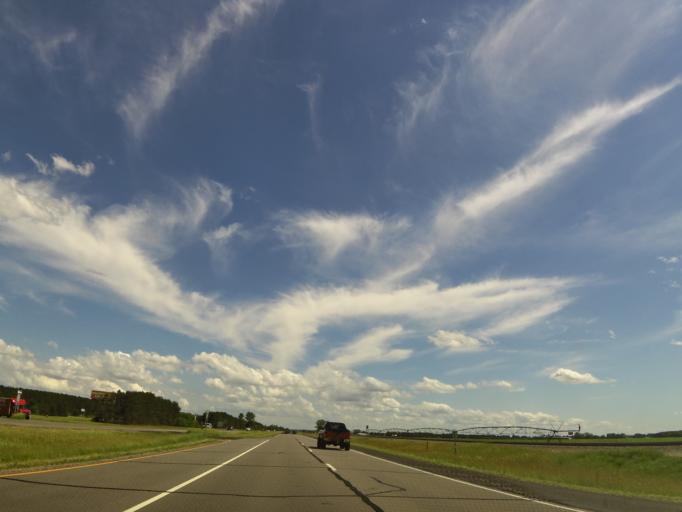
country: US
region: Minnesota
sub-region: Benton County
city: Rice
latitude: 45.7359
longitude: -94.2041
